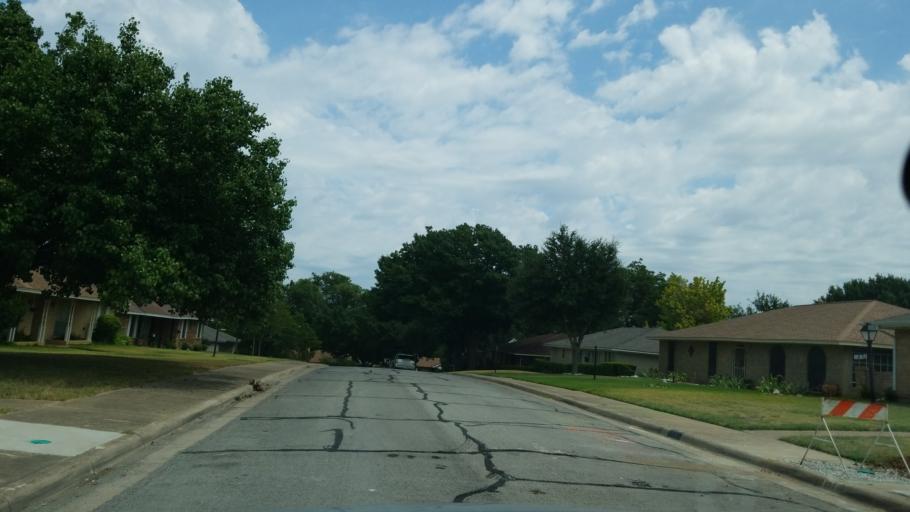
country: US
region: Texas
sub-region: Dallas County
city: Duncanville
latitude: 32.6578
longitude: -96.8483
